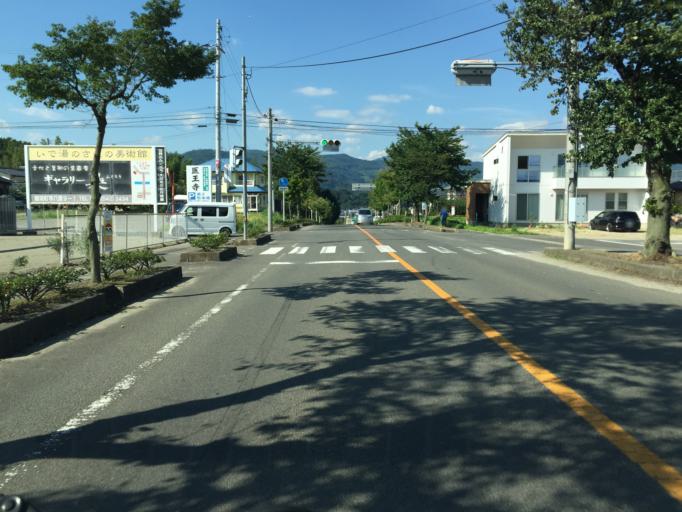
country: JP
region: Fukushima
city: Fukushima-shi
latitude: 37.8203
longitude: 140.4423
